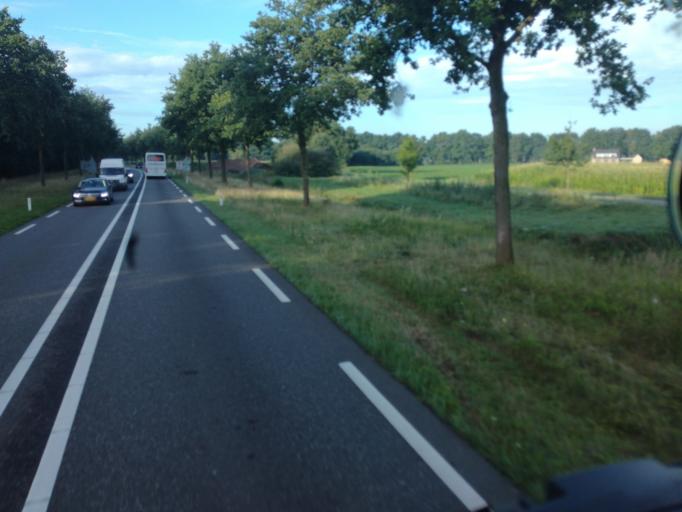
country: NL
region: North Brabant
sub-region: Gemeente Goirle
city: Goirle
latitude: 51.5276
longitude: 5.0426
